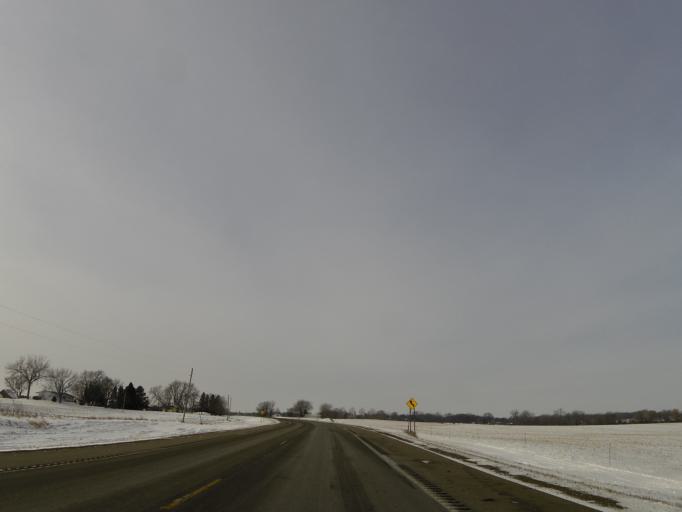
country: US
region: Minnesota
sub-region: Carver County
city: Mayer
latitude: 44.9061
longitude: -93.9607
